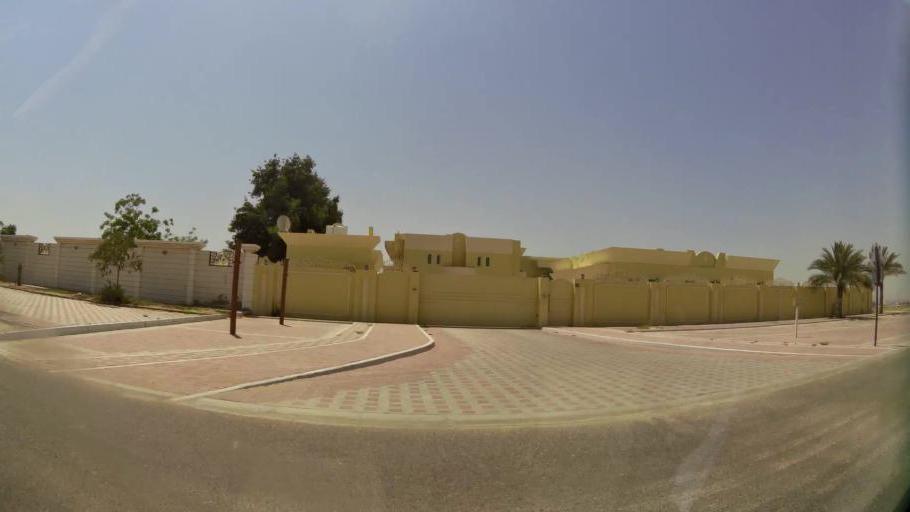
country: AE
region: Ajman
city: Ajman
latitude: 25.4278
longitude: 55.5041
